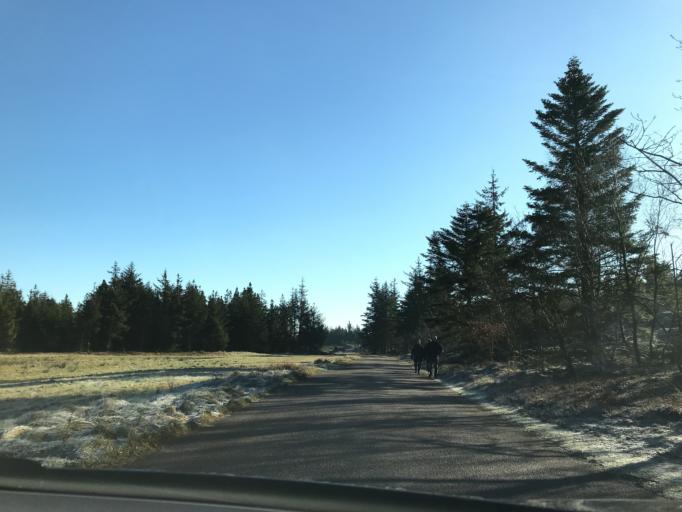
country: DK
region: South Denmark
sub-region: Varde Kommune
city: Oksbol
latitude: 55.7946
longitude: 8.2152
